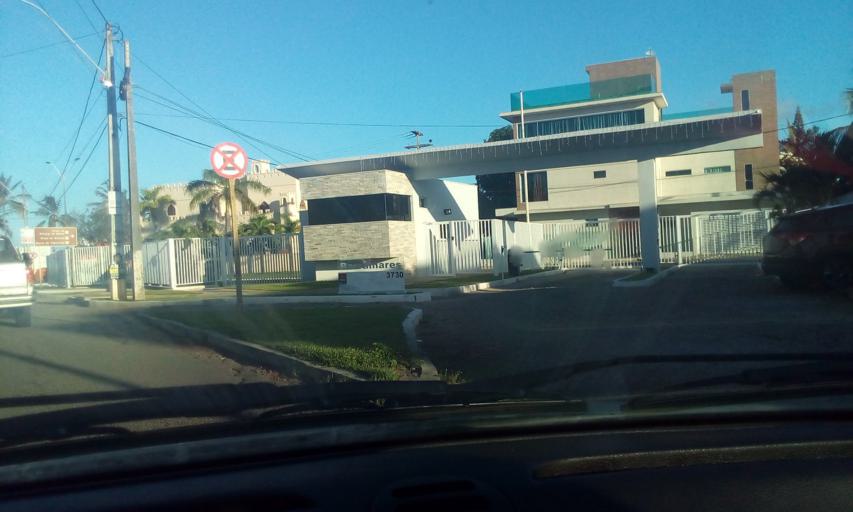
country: BR
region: Rio Grande do Norte
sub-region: Parnamirim
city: Parnamirim
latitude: -5.9633
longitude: -35.1474
